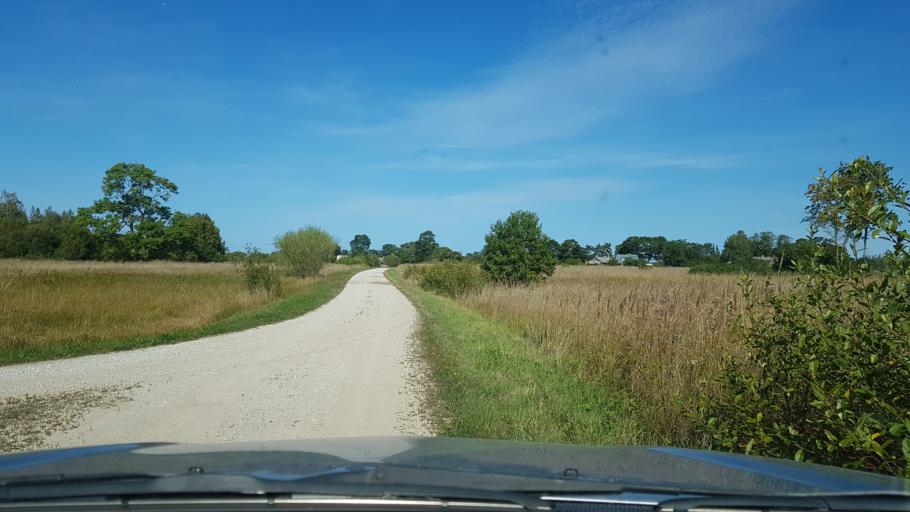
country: EE
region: Ida-Virumaa
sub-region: Sillamaee linn
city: Sillamae
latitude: 59.3807
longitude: 27.8108
